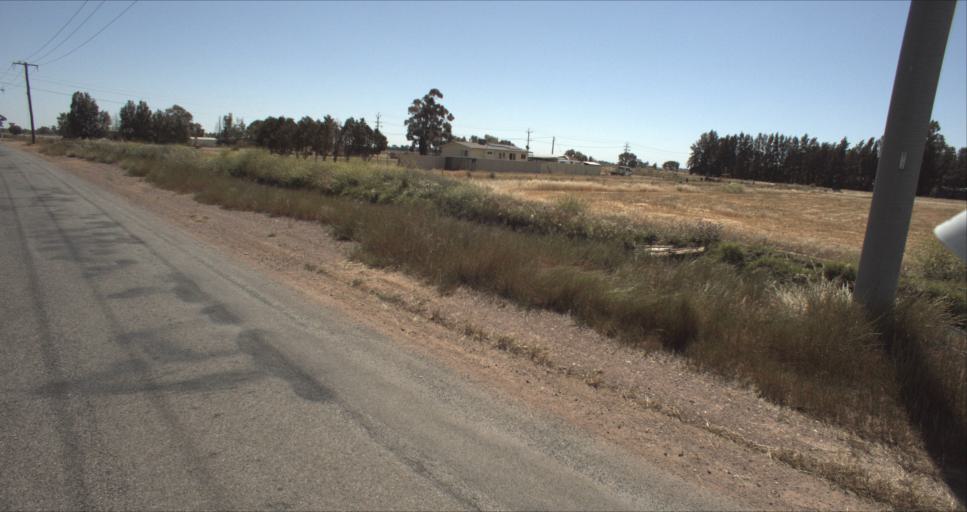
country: AU
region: New South Wales
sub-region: Leeton
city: Leeton
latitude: -34.5322
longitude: 146.3900
